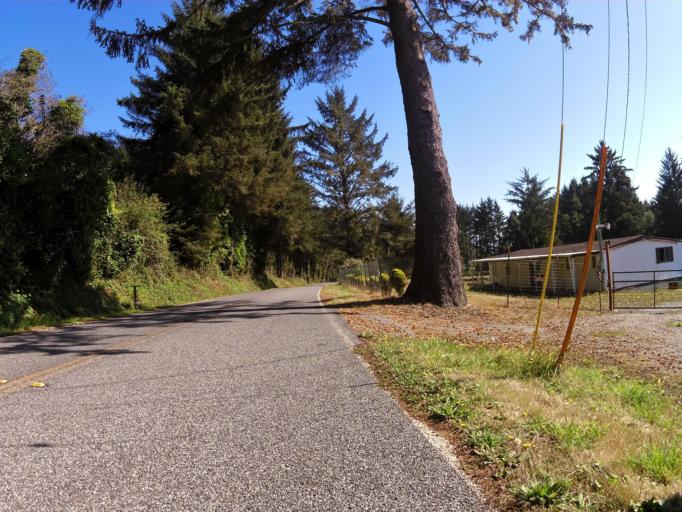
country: US
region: Oregon
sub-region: Curry County
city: Harbor
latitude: 41.9518
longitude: -124.1998
